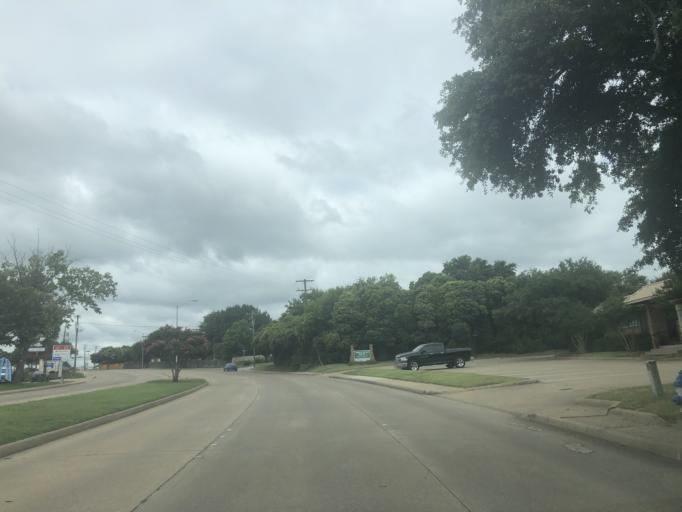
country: US
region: Texas
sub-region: Dallas County
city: Duncanville
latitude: 32.6471
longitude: -96.9195
